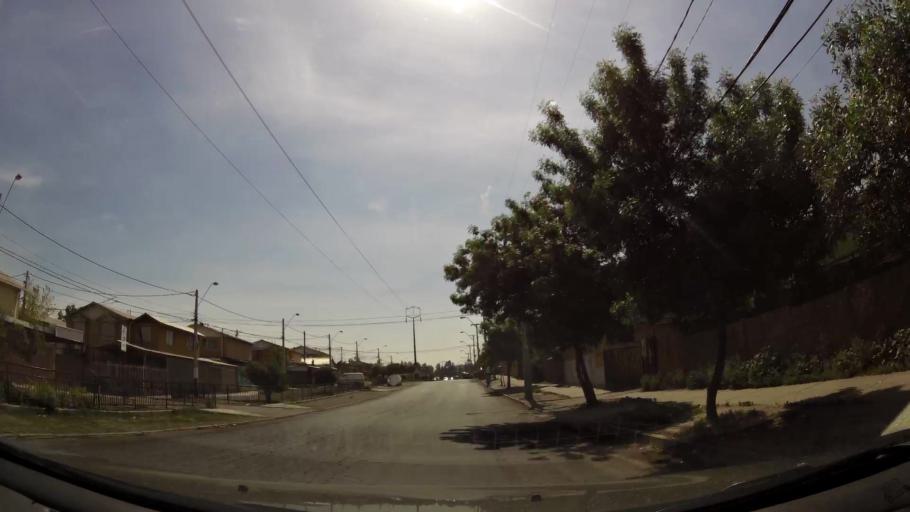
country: CL
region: Santiago Metropolitan
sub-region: Provincia de Cordillera
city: Puente Alto
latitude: -33.6132
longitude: -70.5551
